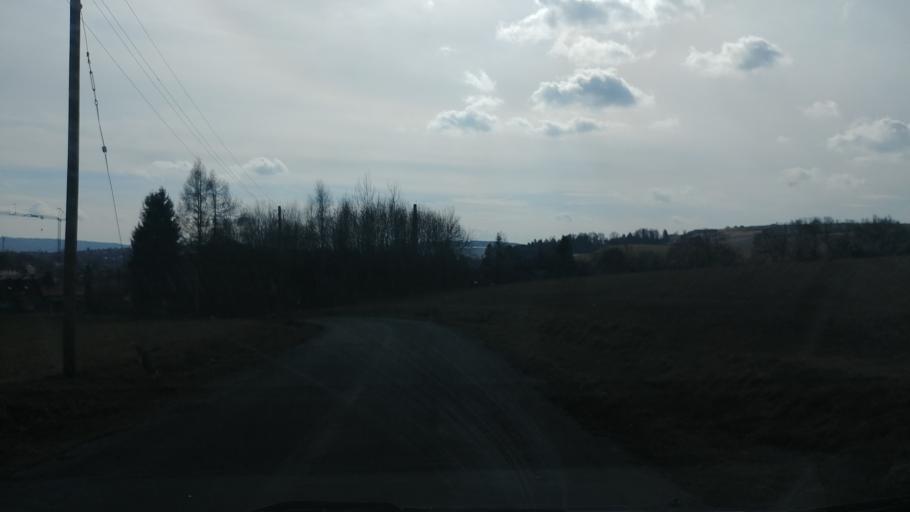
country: DE
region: Lower Saxony
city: Uslar
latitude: 51.6689
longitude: 9.6227
